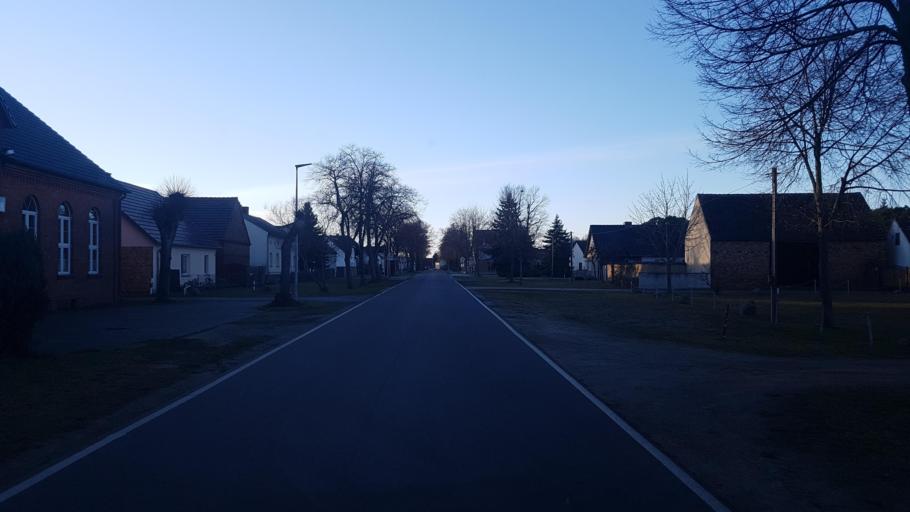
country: DE
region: Brandenburg
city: Drehnow
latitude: 51.8665
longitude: 14.3580
